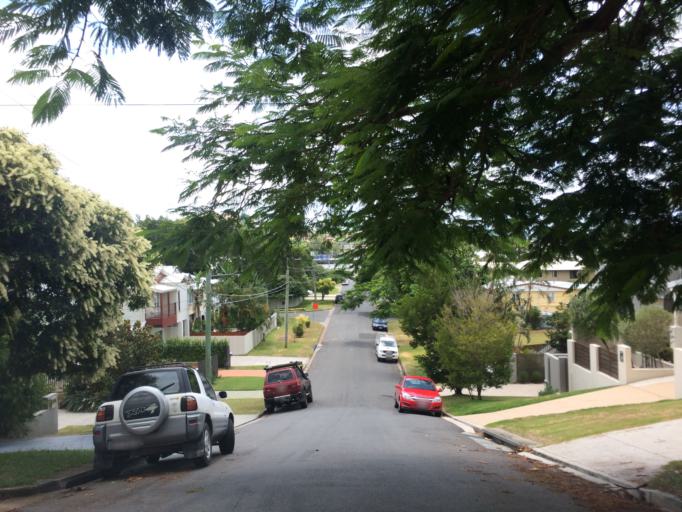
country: AU
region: Queensland
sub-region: Brisbane
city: Ascot
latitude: -27.4454
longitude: 153.0598
